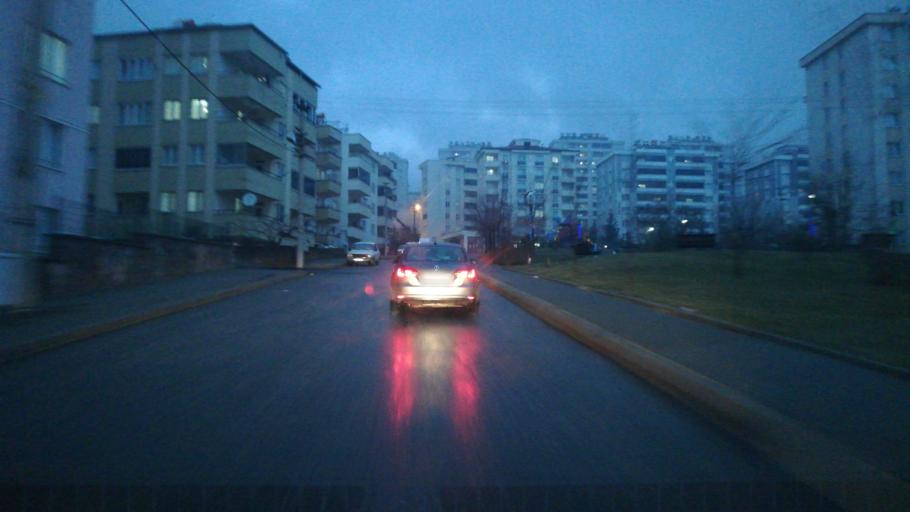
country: TR
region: Kahramanmaras
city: Kahramanmaras
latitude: 37.5958
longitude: 36.8931
